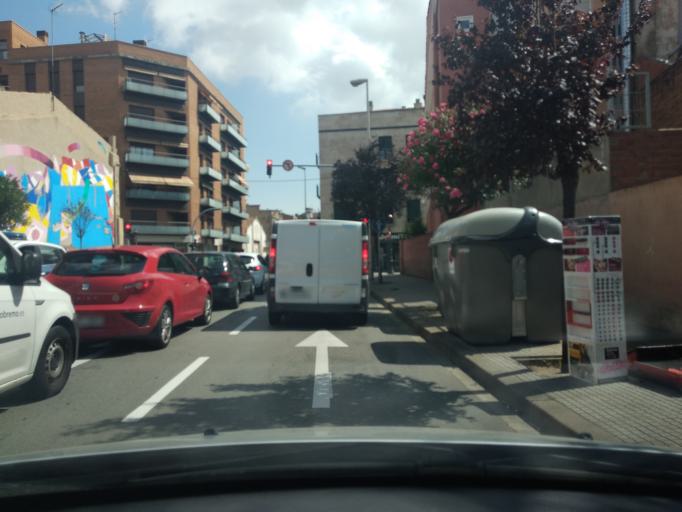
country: ES
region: Catalonia
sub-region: Provincia de Barcelona
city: Granollers
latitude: 41.6138
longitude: 2.2899
